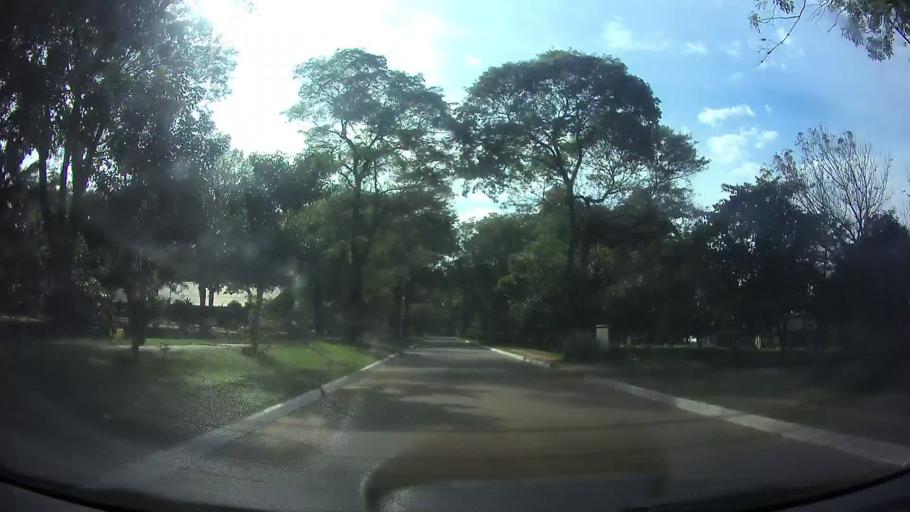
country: PY
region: Central
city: Fernando de la Mora
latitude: -25.3375
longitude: -57.5178
